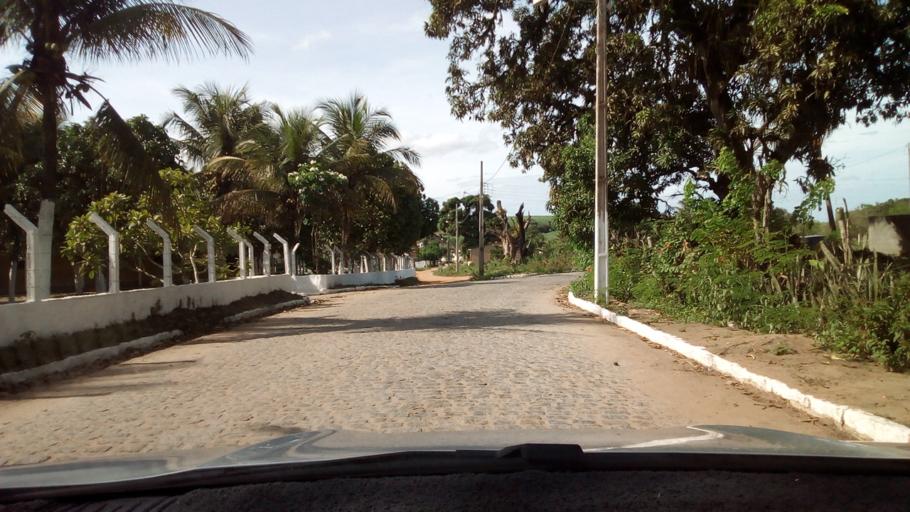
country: BR
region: Paraiba
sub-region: Santa Rita
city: Santa Rita
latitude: -7.0837
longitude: -34.9694
